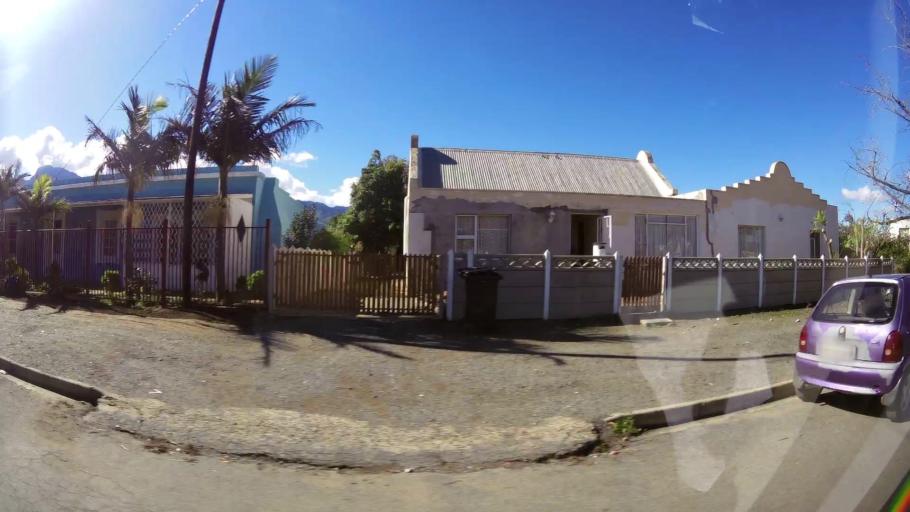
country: ZA
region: Western Cape
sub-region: Cape Winelands District Municipality
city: Ashton
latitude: -33.7969
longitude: 19.8843
